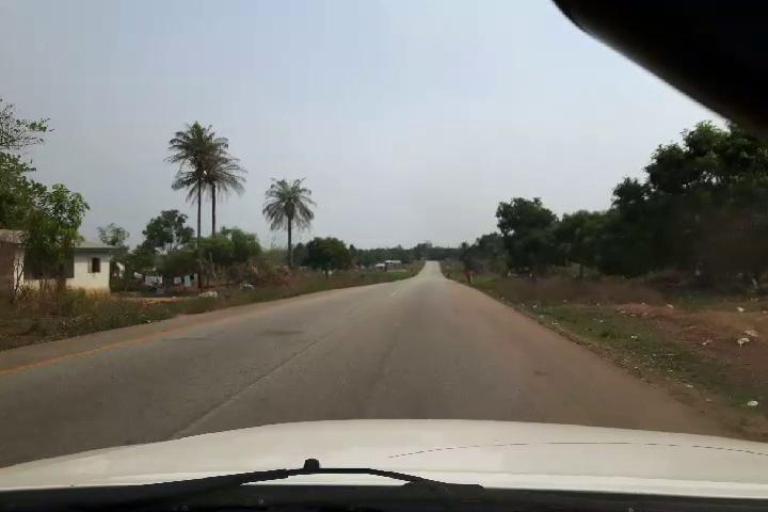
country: SL
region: Southern Province
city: Largo
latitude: 8.3149
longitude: -12.2175
